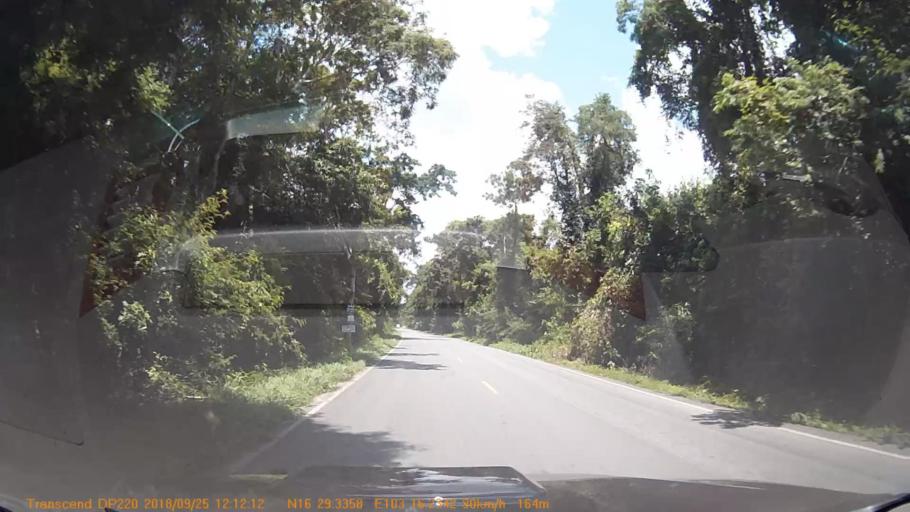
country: TH
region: Kalasin
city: Huai Mek
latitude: 16.4890
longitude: 103.2706
